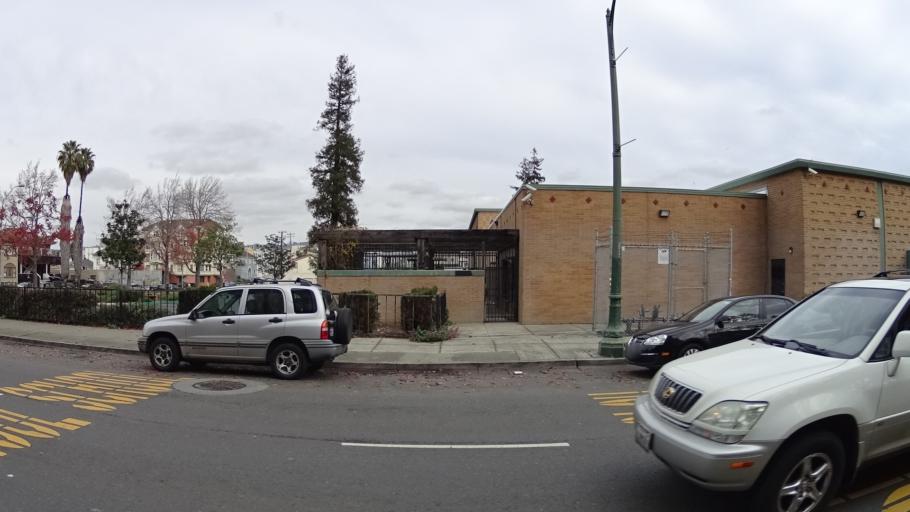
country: US
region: California
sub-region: Alameda County
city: Oakland
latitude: 37.7962
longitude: -122.2562
